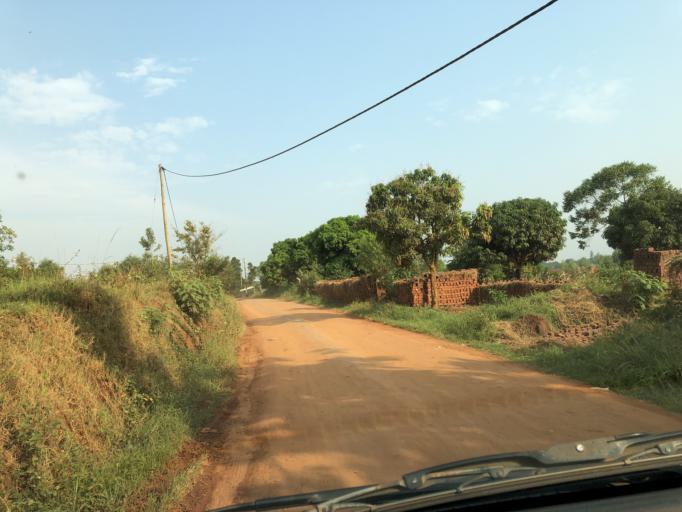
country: UG
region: Central Region
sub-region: Wakiso District
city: Bweyogerere
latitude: 0.4734
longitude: 32.6353
